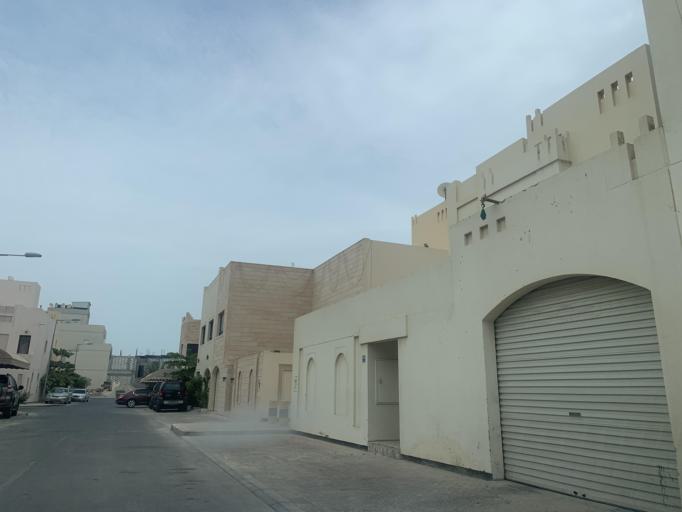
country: BH
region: Muharraq
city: Al Muharraq
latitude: 26.2834
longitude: 50.6416
